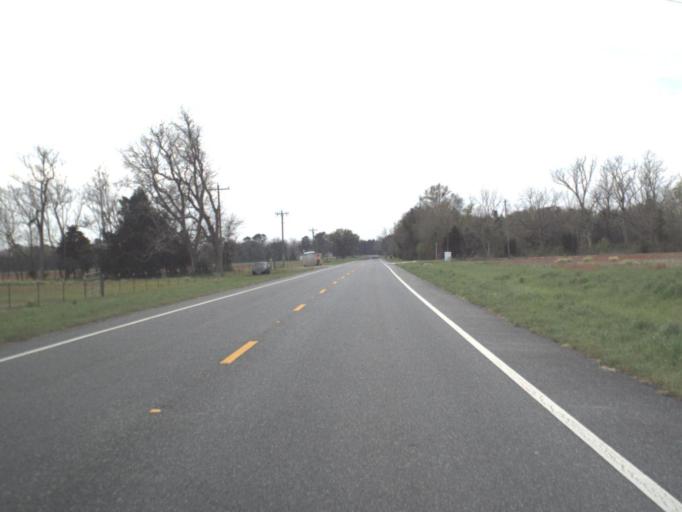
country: US
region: Florida
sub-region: Calhoun County
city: Blountstown
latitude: 30.4894
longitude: -85.2001
